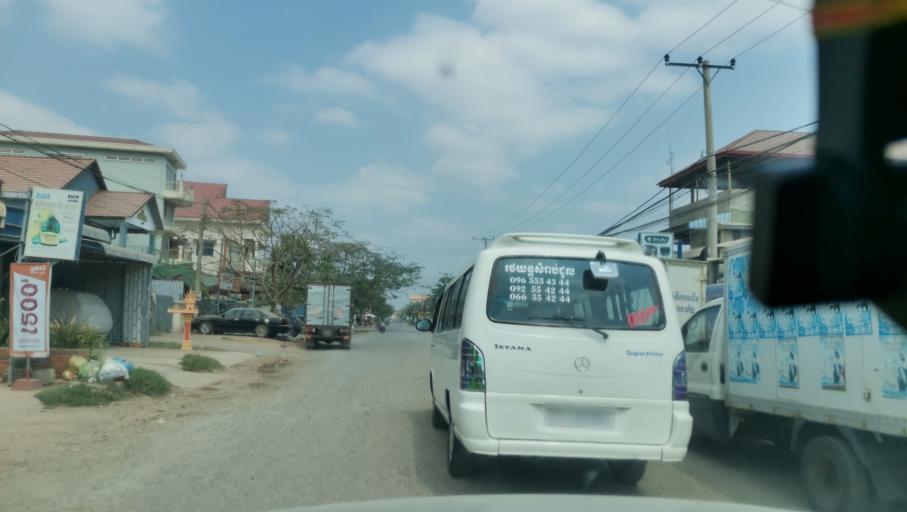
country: KH
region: Battambang
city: Battambang
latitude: 13.1091
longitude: 103.1957
